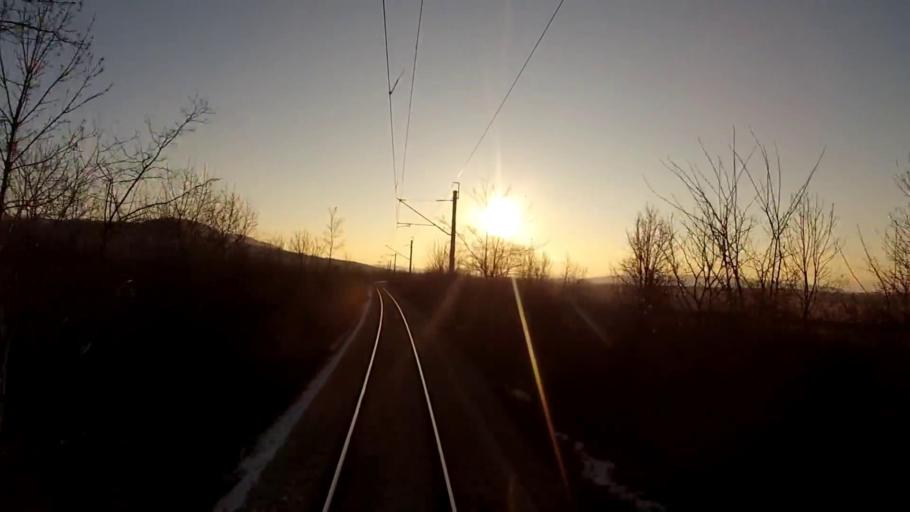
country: BG
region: Sofiya
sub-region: Obshtina Dragoman
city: Dragoman
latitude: 42.8958
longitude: 22.9658
